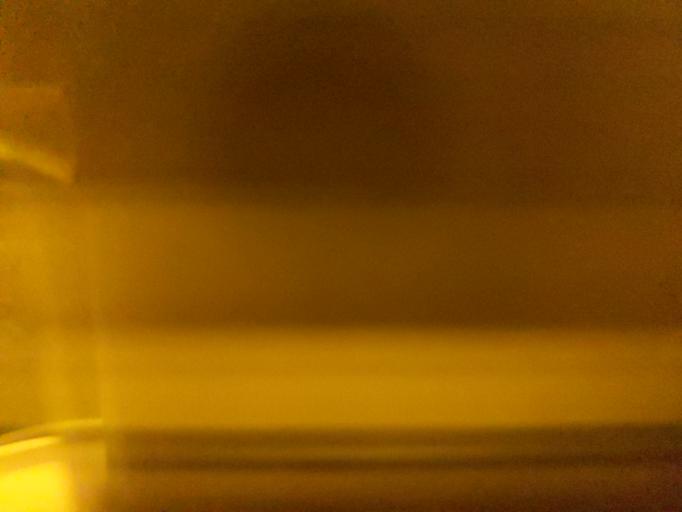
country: JP
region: Miyagi
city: Shiroishi
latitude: 38.0283
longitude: 140.6700
